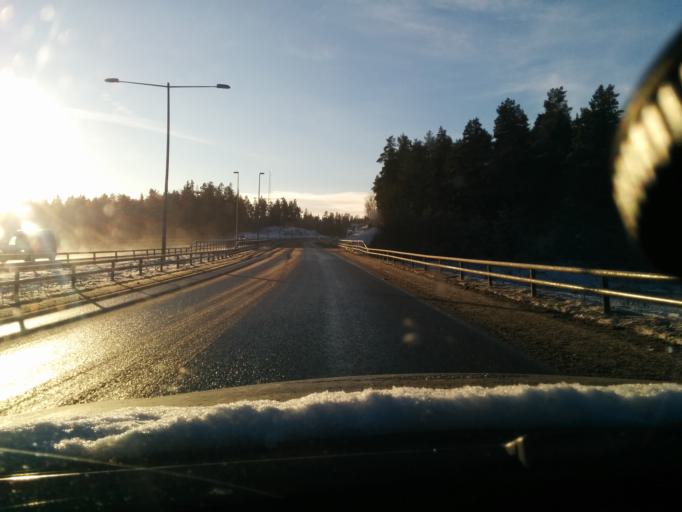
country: SE
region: Stockholm
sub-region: Sollentuna Kommun
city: Sollentuna
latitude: 59.4708
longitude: 17.9844
